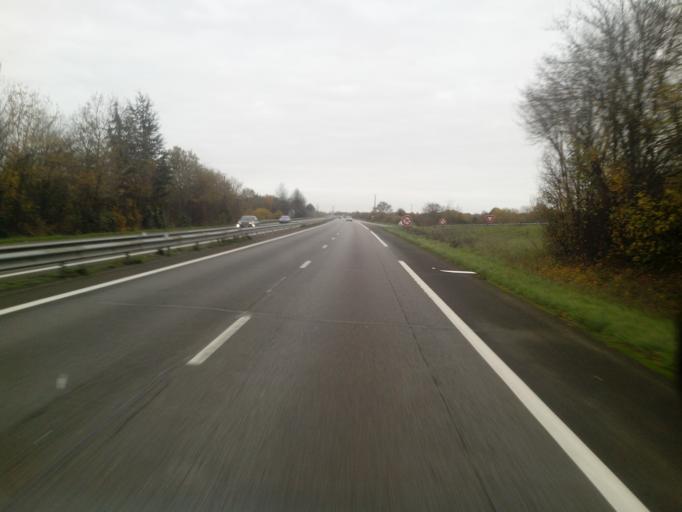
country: FR
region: Pays de la Loire
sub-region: Departement de la Loire-Atlantique
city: Heric
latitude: 47.4465
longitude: -1.6413
